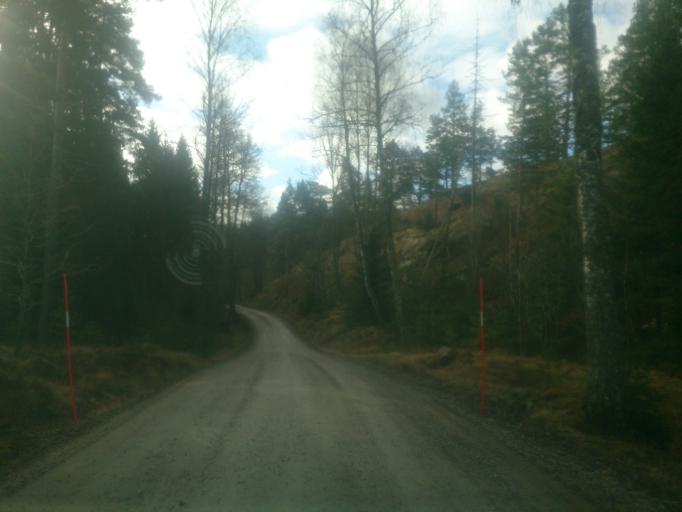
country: SE
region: OEstergoetland
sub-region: Atvidabergs Kommun
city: Atvidaberg
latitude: 58.2156
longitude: 16.1703
